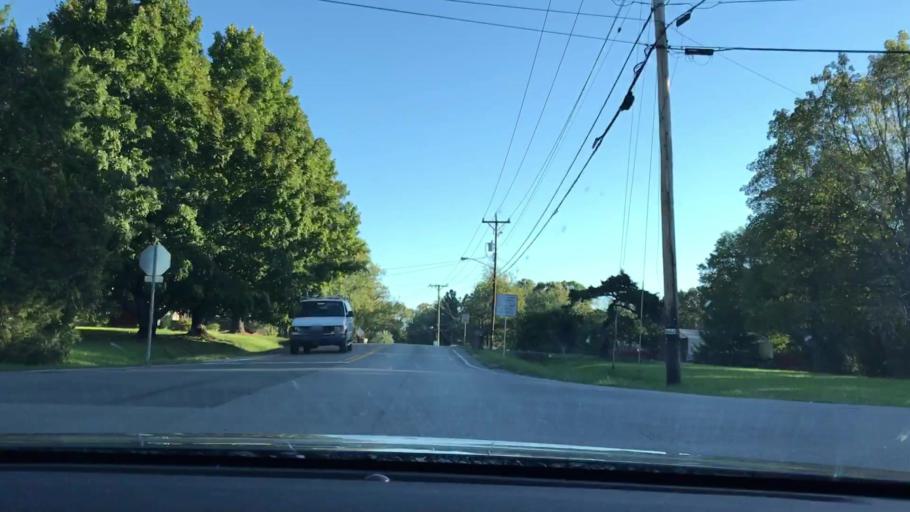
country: US
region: Tennessee
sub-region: Davidson County
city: Oak Hill
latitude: 36.0629
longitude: -86.6972
